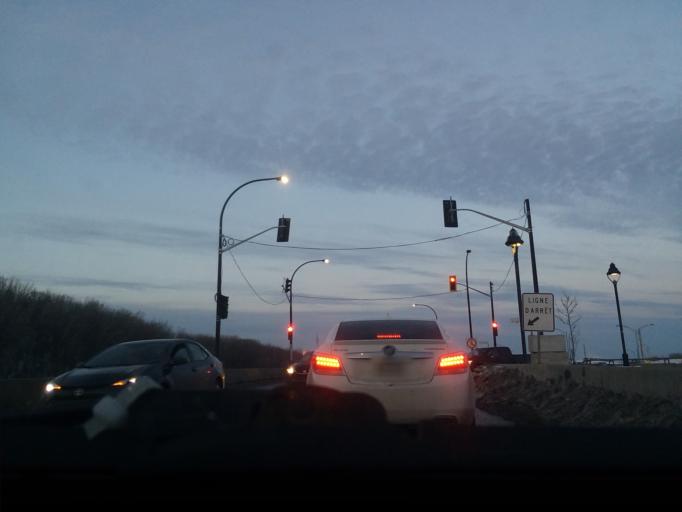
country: CA
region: Quebec
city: Montreal-Ouest
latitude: 45.4541
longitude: -73.6285
